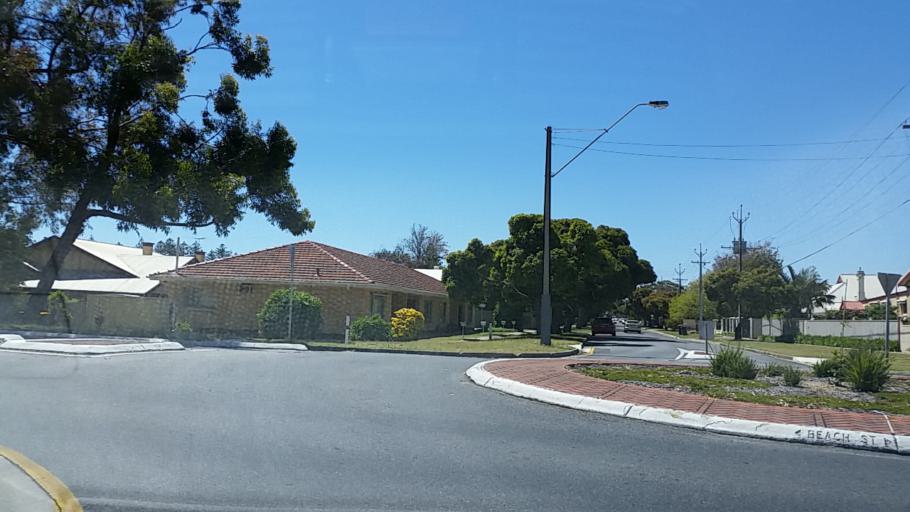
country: AU
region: South Australia
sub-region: Charles Sturt
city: Grange
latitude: -34.9051
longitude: 138.4952
